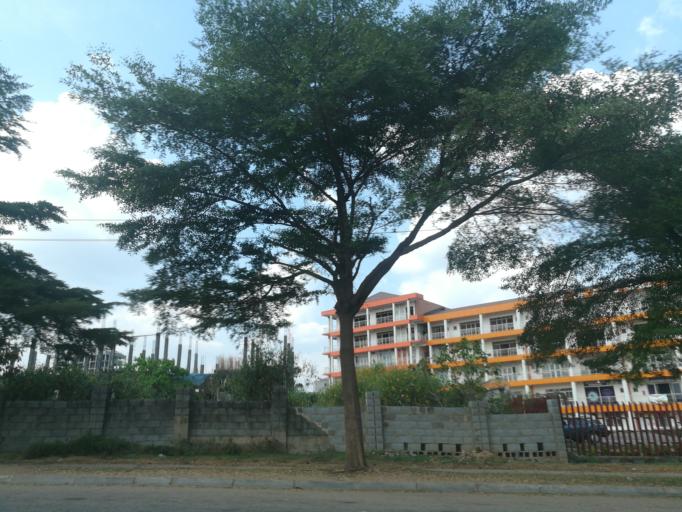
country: NG
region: Abuja Federal Capital Territory
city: Abuja
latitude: 9.0666
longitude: 7.4348
